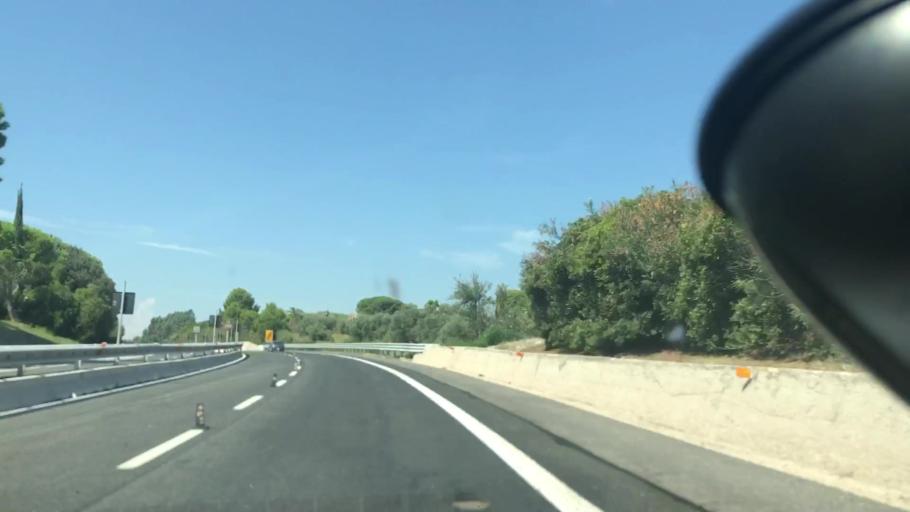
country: IT
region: Abruzzo
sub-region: Provincia di Chieti
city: Marina di Vasto
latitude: 42.0732
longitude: 14.7209
